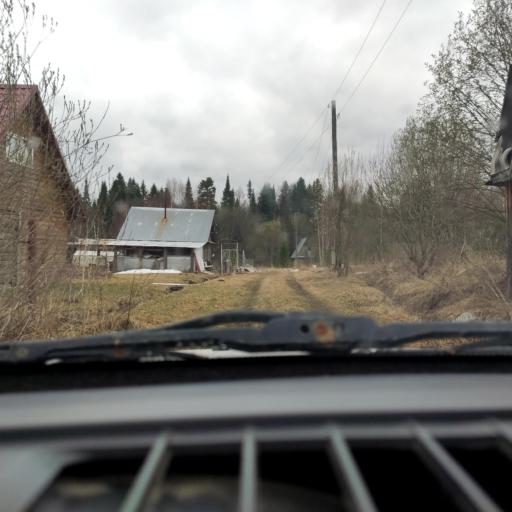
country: RU
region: Perm
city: Kultayevo
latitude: 57.8256
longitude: 55.7747
